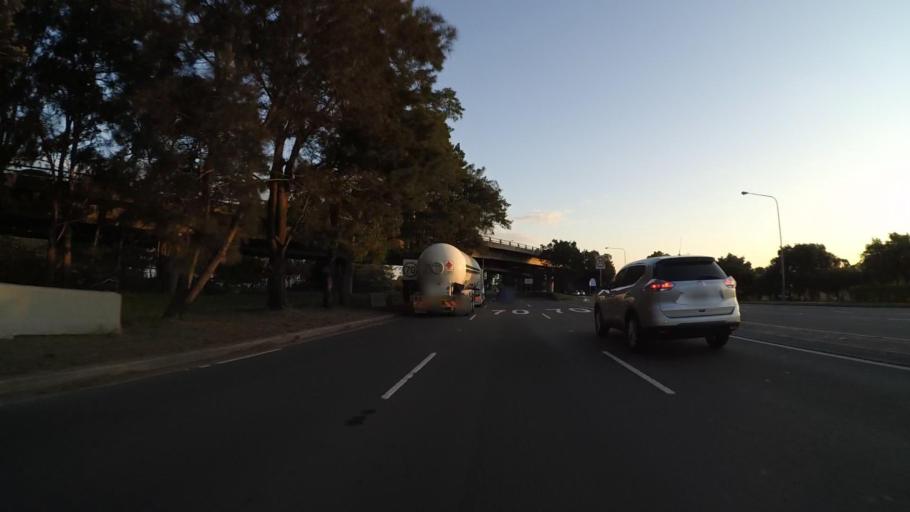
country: AU
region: New South Wales
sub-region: Botany Bay
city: Botany
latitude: -33.9390
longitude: 151.1929
